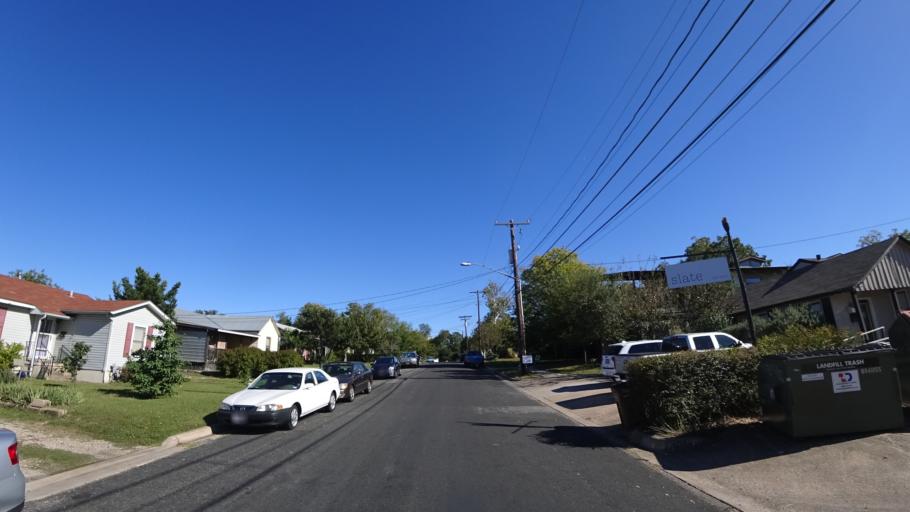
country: US
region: Texas
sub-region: Travis County
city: Austin
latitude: 30.3223
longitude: -97.7388
